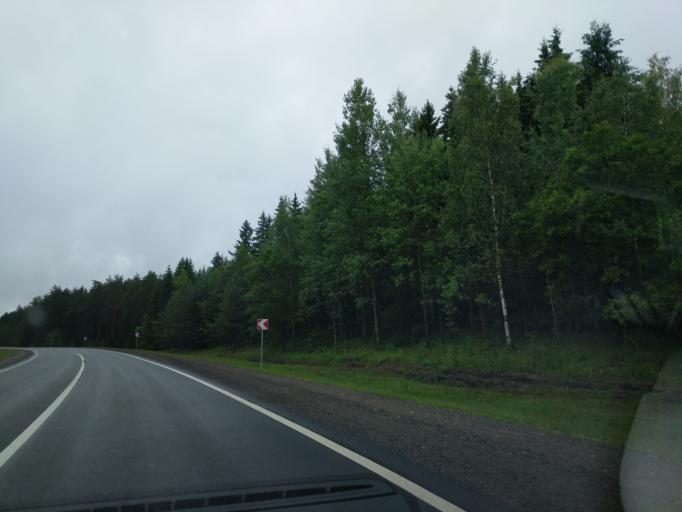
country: BY
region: Minsk
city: Syomkava
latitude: 54.1949
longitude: 27.4996
